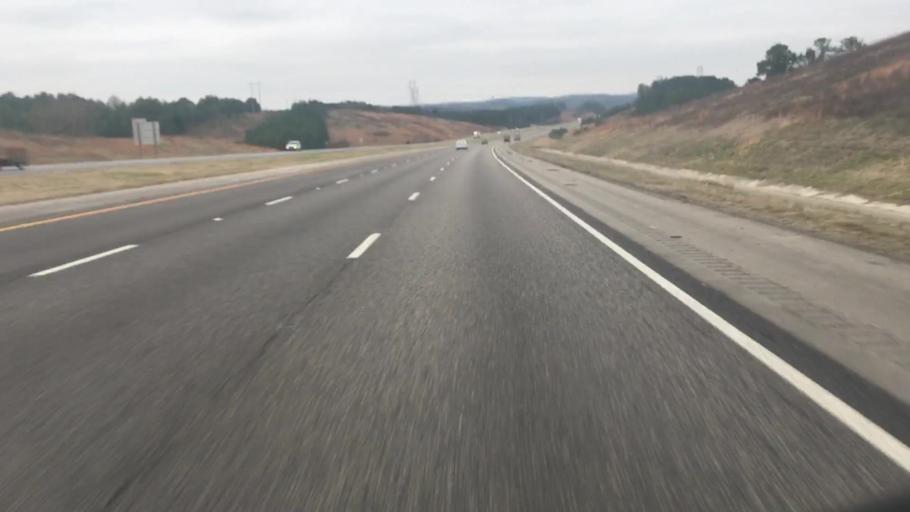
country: US
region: Alabama
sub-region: Jefferson County
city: Graysville
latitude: 33.6494
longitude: -86.9959
